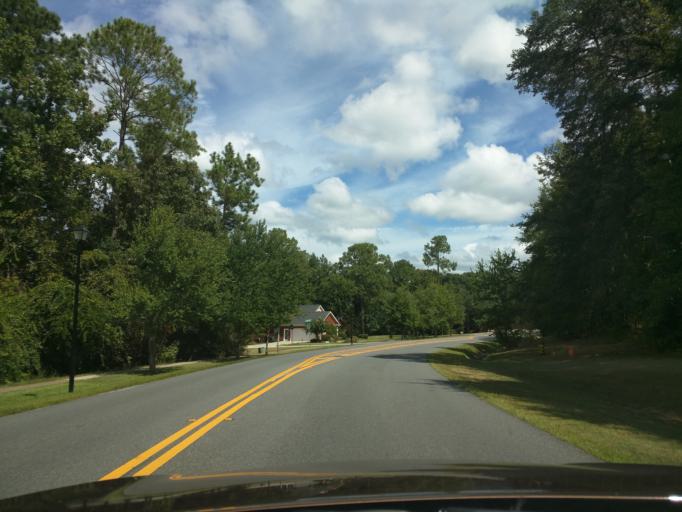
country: US
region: Florida
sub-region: Leon County
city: Tallahassee
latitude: 30.5856
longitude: -84.2558
